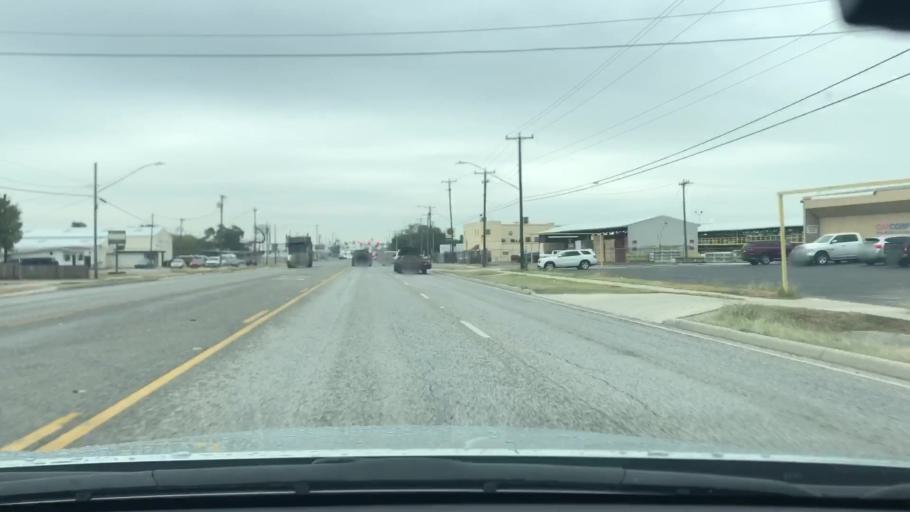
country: US
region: Texas
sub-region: Bexar County
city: Kirby
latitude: 29.4437
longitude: -98.4050
